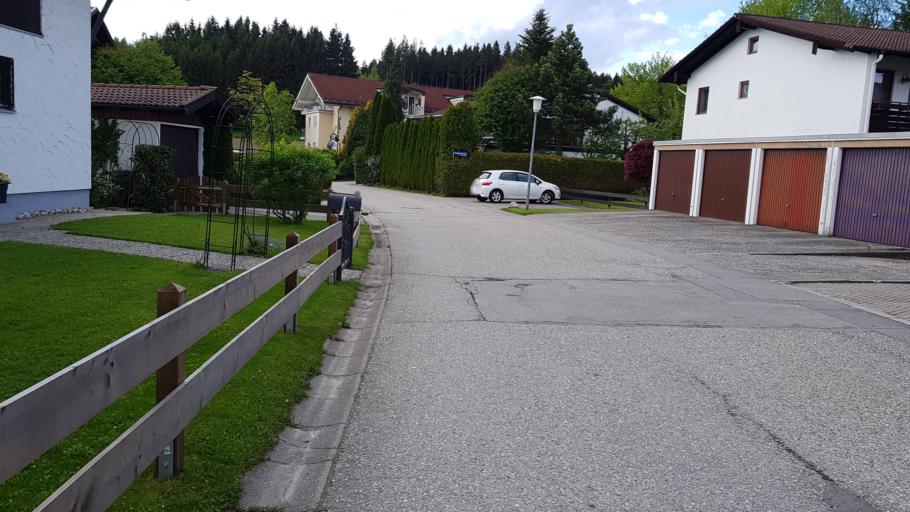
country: DE
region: Bavaria
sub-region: Upper Bavaria
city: Bad Endorf
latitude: 47.9127
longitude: 12.3038
